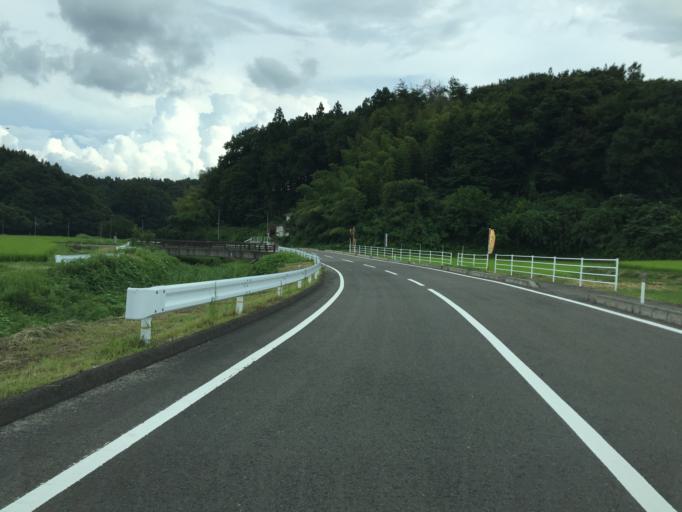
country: JP
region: Fukushima
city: Fukushima-shi
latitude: 37.6851
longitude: 140.5204
